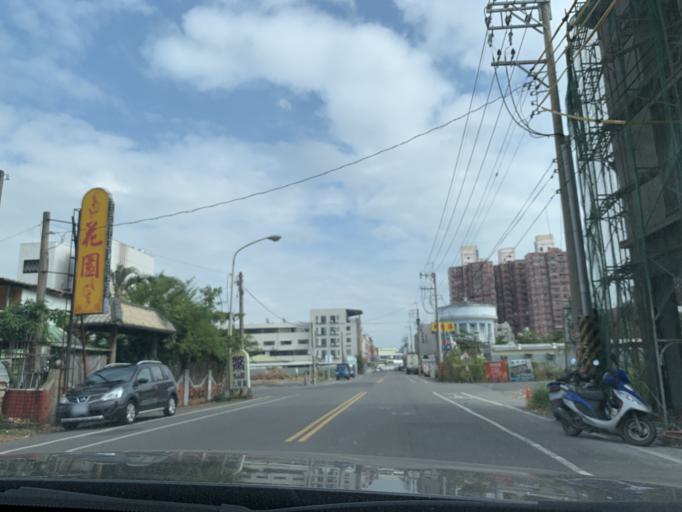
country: TW
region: Taiwan
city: Fengshan
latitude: 22.4669
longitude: 120.4604
